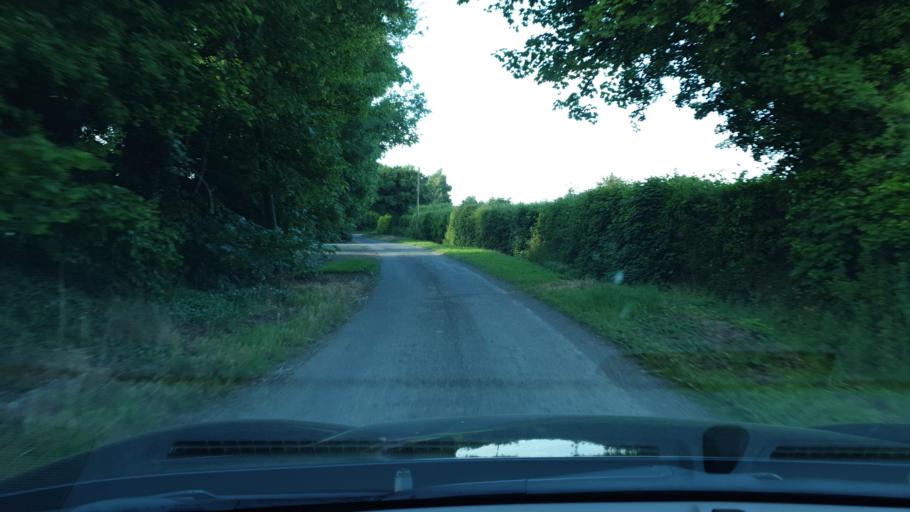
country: IE
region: Leinster
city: Hartstown
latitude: 53.4365
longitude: -6.4029
